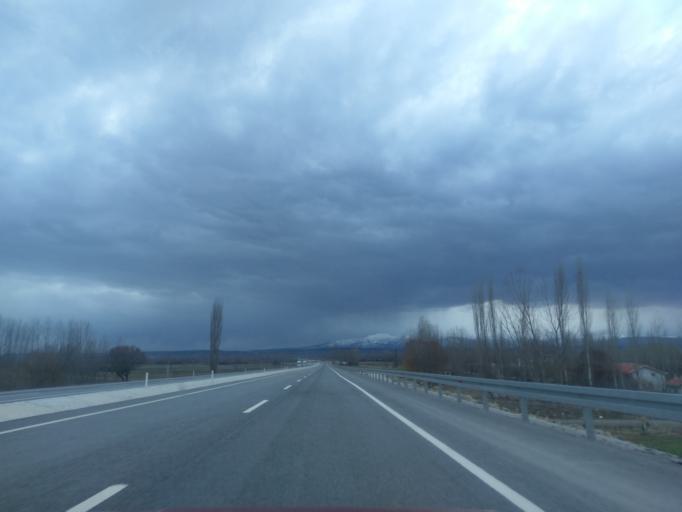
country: TR
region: Kuetahya
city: Cavdarhisar
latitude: 39.2163
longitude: 29.6637
